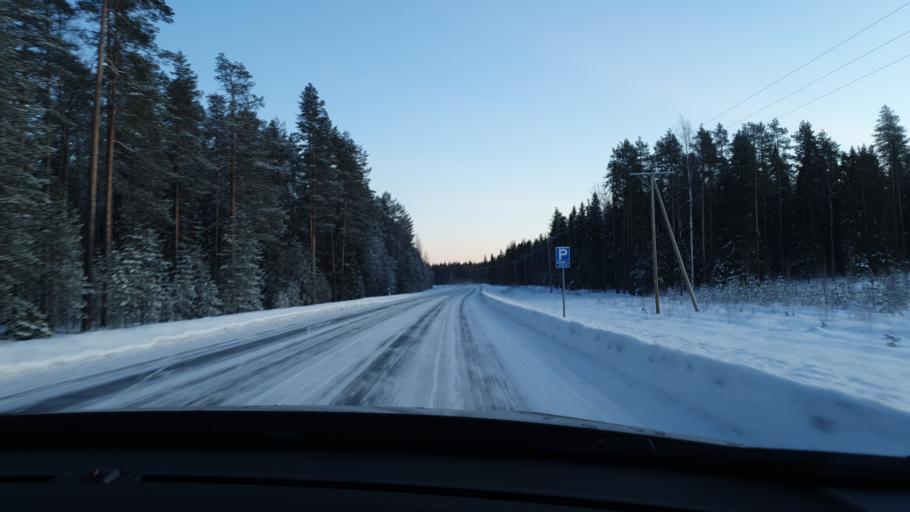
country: FI
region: North Karelia
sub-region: Pielisen Karjala
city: Valtimo
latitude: 64.0860
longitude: 28.9795
